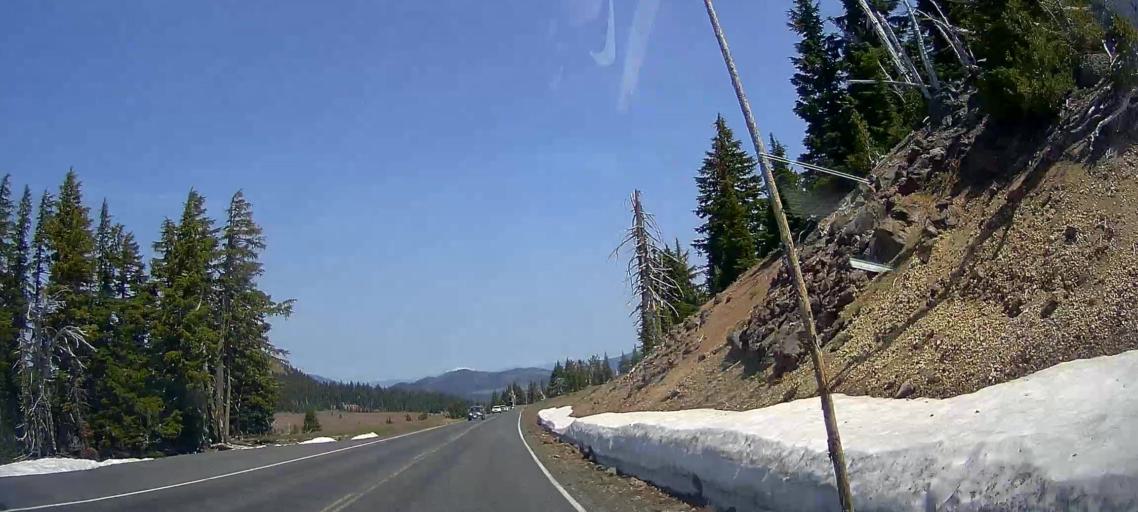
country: US
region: Oregon
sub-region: Jackson County
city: Shady Cove
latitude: 42.9780
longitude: -122.1530
